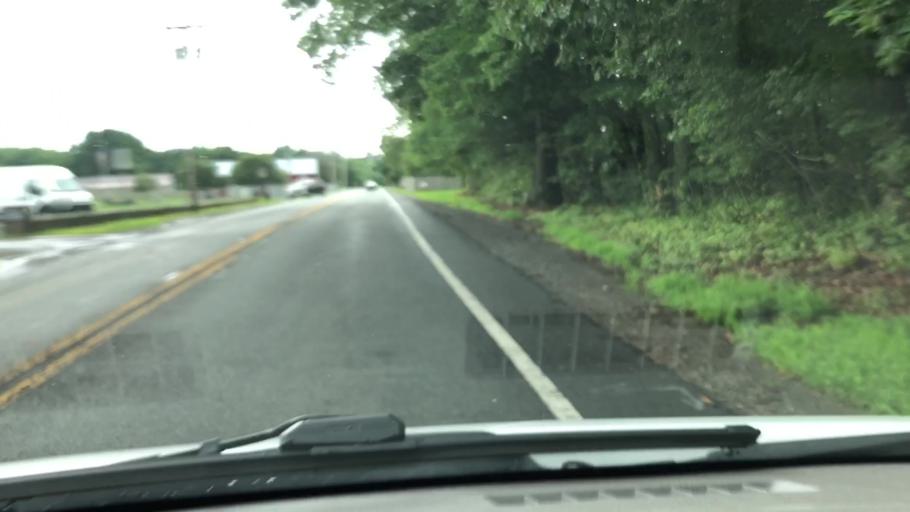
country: US
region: Massachusetts
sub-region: Franklin County
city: Whately
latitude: 42.4188
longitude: -72.6213
